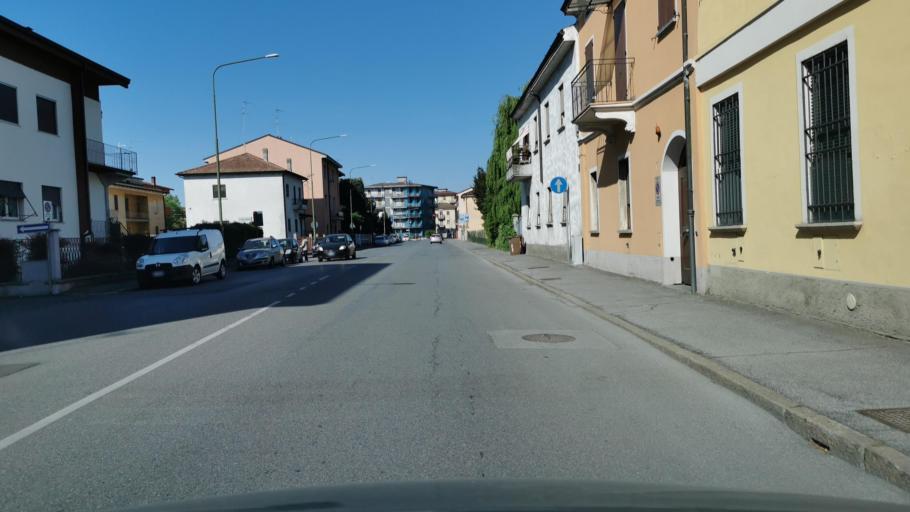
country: IT
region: Lombardy
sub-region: Provincia di Cremona
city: Cremona
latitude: 45.1284
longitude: 10.0338
